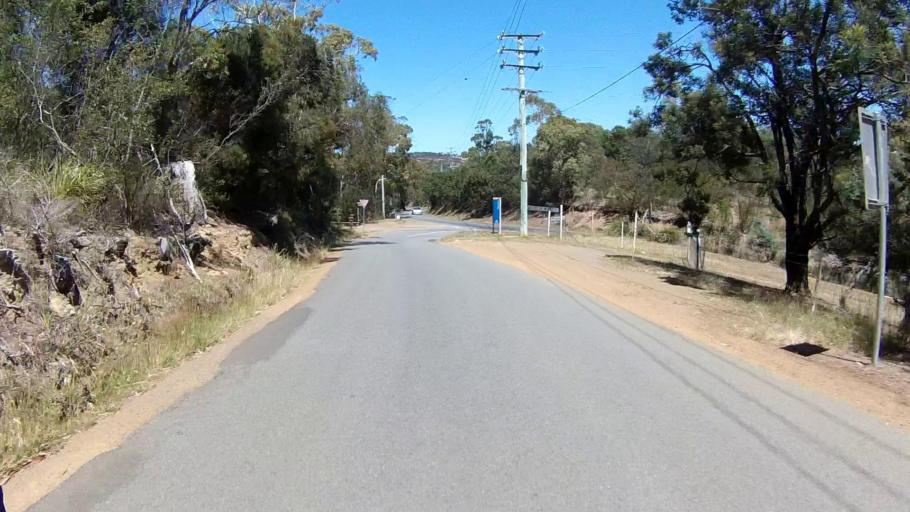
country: AU
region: Tasmania
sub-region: Clarence
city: Howrah
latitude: -42.8555
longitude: 147.4208
